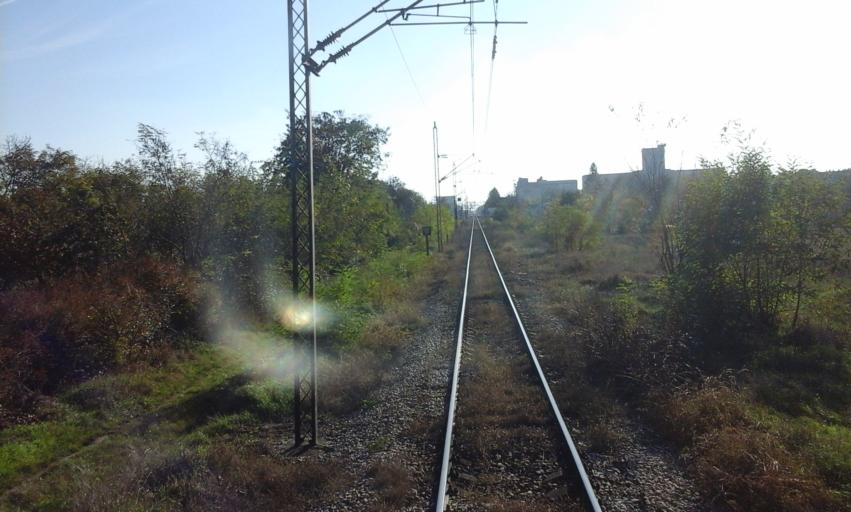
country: RS
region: Autonomna Pokrajina Vojvodina
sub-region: Severnobacki Okrug
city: Backa Topola
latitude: 45.8229
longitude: 19.6503
